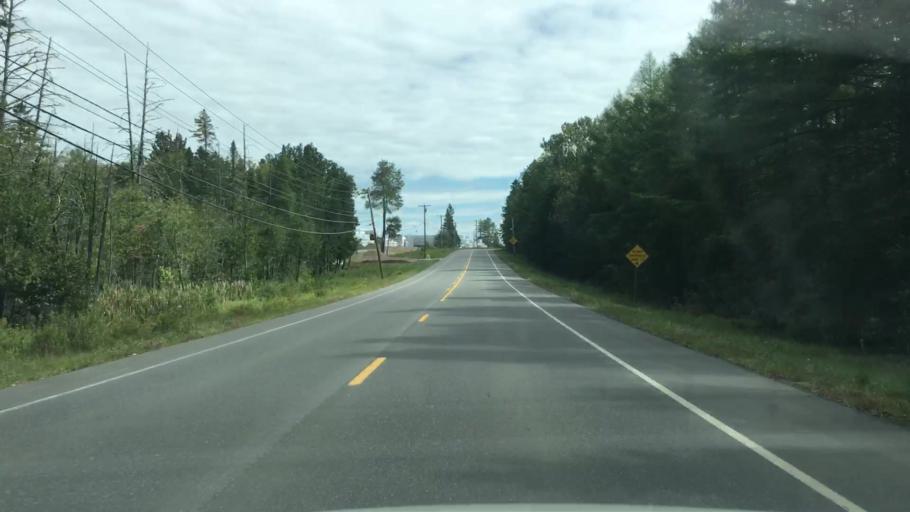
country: US
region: Maine
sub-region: Piscataquis County
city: Dover-Foxcroft
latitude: 45.2000
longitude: -69.2004
